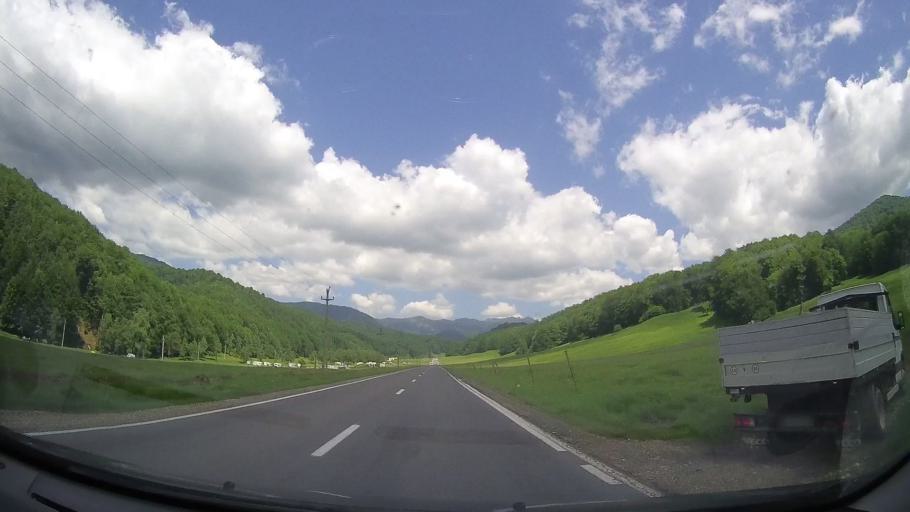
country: RO
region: Prahova
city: Maneciu
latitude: 45.4212
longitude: 25.9426
